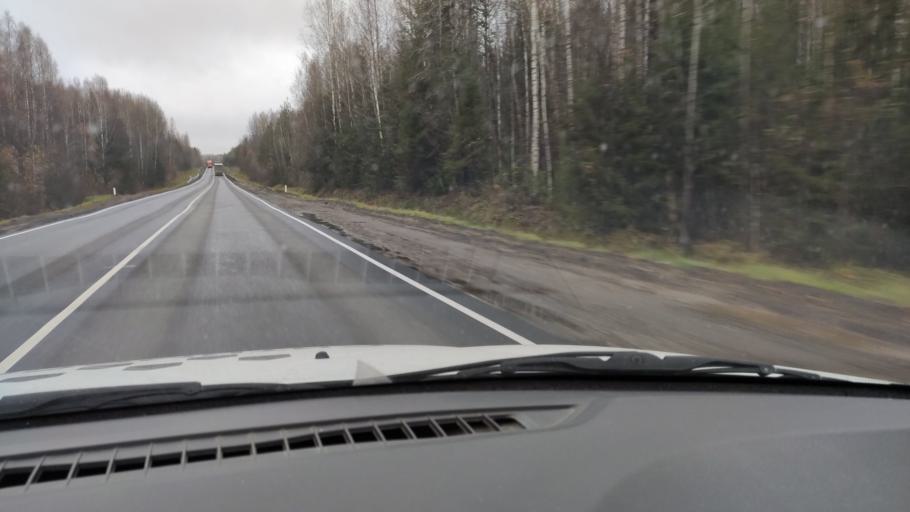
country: RU
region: Kirov
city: Omutninsk
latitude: 58.7378
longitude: 52.0702
